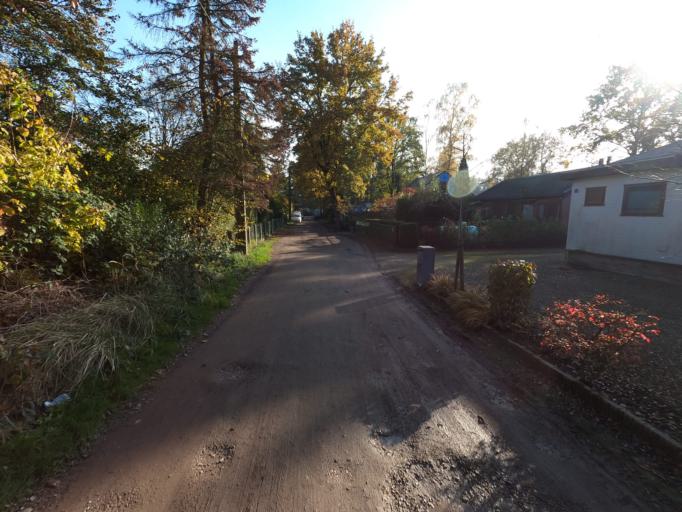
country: BE
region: Flanders
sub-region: Provincie Antwerpen
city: Wuustwezel
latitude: 51.3437
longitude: 4.5448
